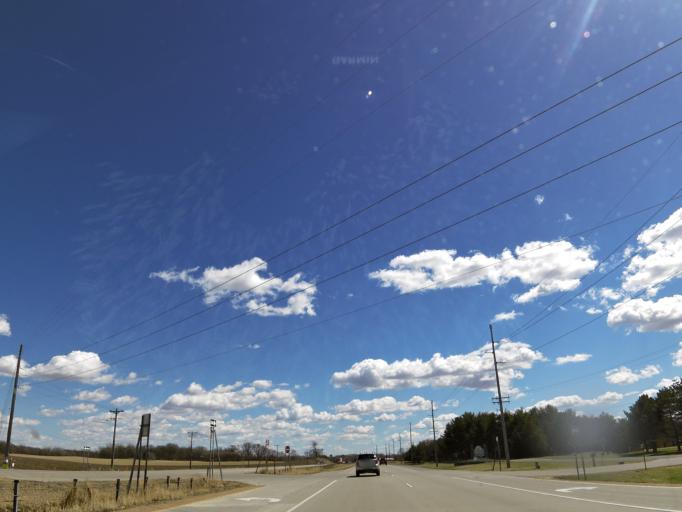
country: US
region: Minnesota
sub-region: Dakota County
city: Hastings
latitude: 44.7904
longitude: -92.8843
